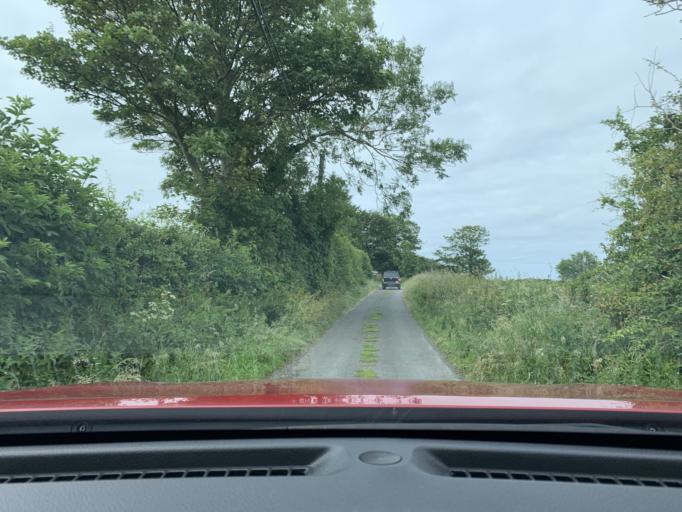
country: IE
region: Connaught
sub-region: Sligo
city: Sligo
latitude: 54.3770
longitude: -8.5200
